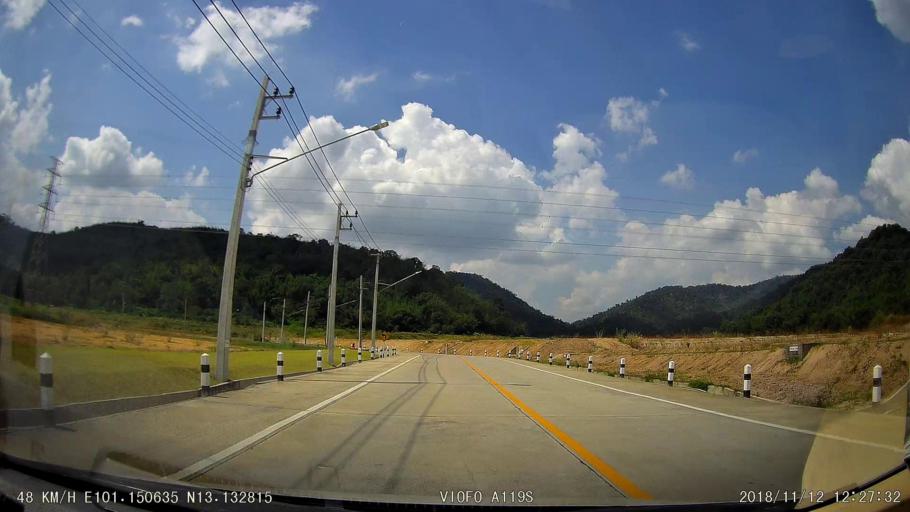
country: TH
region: Chon Buri
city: Ban Talat Bueng
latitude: 13.1328
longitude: 101.1503
